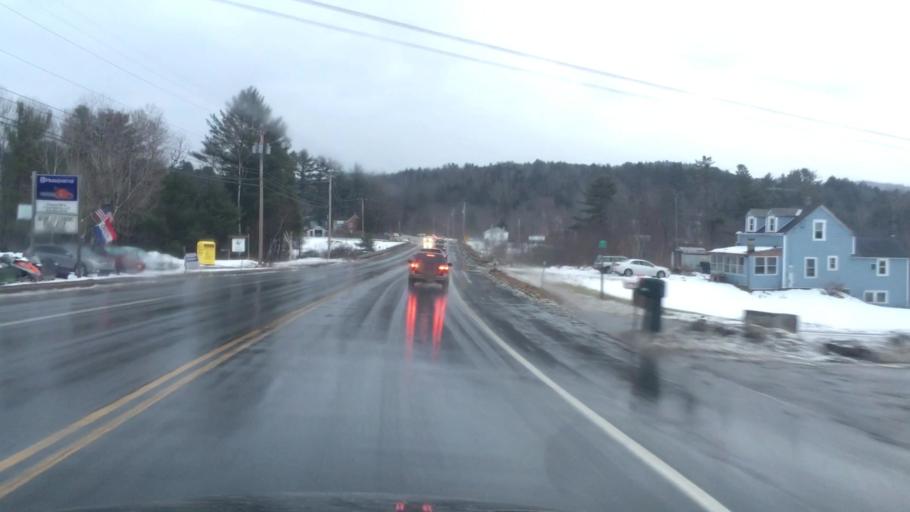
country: US
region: New Hampshire
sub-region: Sullivan County
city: Newport
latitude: 43.3634
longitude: -72.2269
